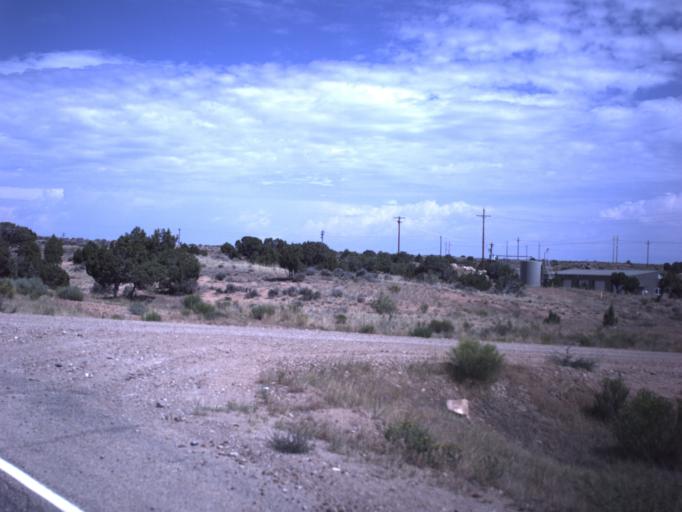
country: US
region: Utah
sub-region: Uintah County
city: Naples
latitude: 40.1818
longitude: -109.3257
